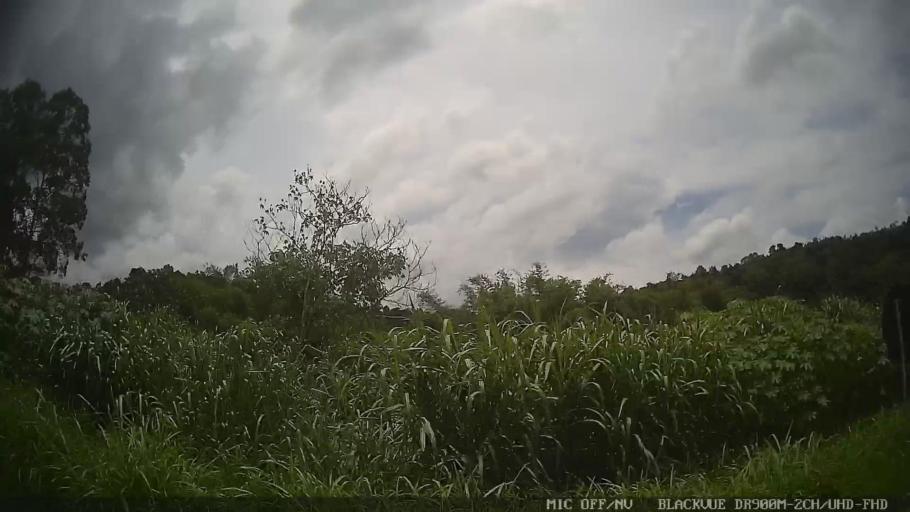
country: BR
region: Sao Paulo
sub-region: Aruja
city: Aruja
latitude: -23.3836
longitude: -46.2653
